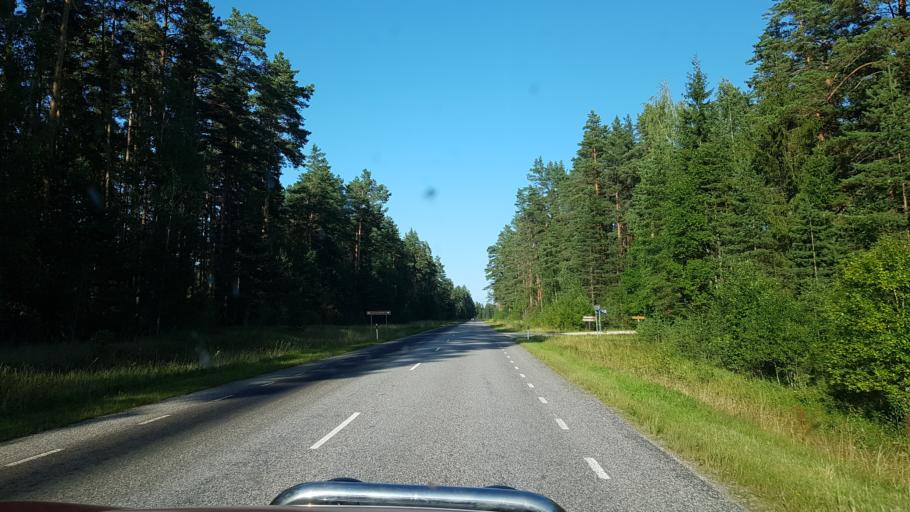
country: RU
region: Pskov
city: Pechory
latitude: 57.8180
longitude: 27.3408
